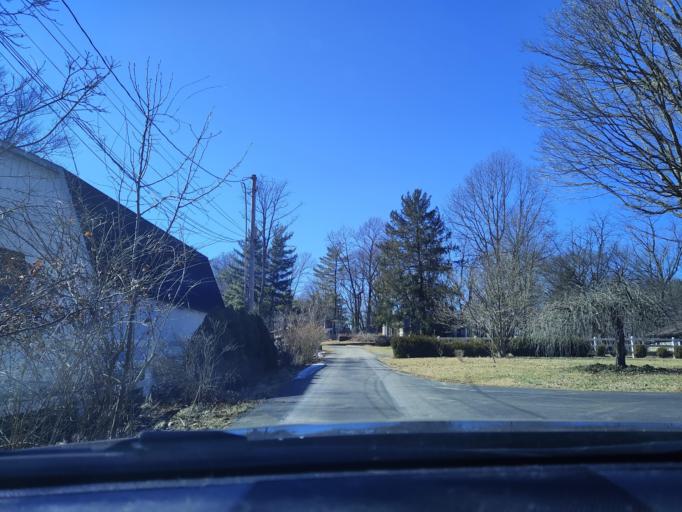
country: US
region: Indiana
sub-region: Hamilton County
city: Carmel
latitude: 39.9443
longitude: -86.1328
